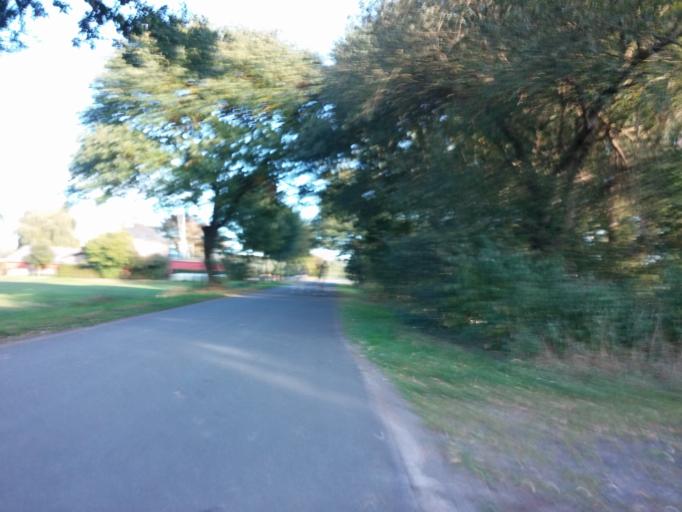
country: DE
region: North Rhine-Westphalia
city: Marl
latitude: 51.6338
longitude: 7.0282
